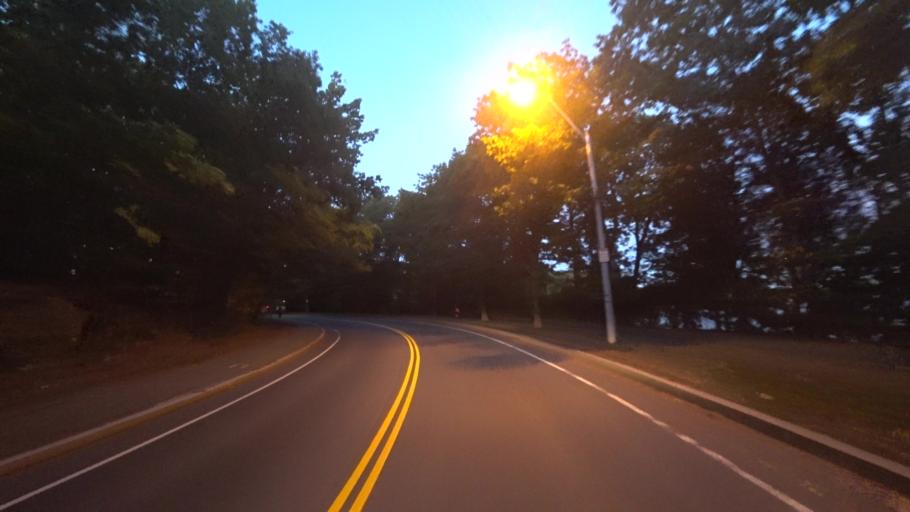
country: US
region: Massachusetts
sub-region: Middlesex County
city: Watertown
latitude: 42.3365
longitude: -71.1623
